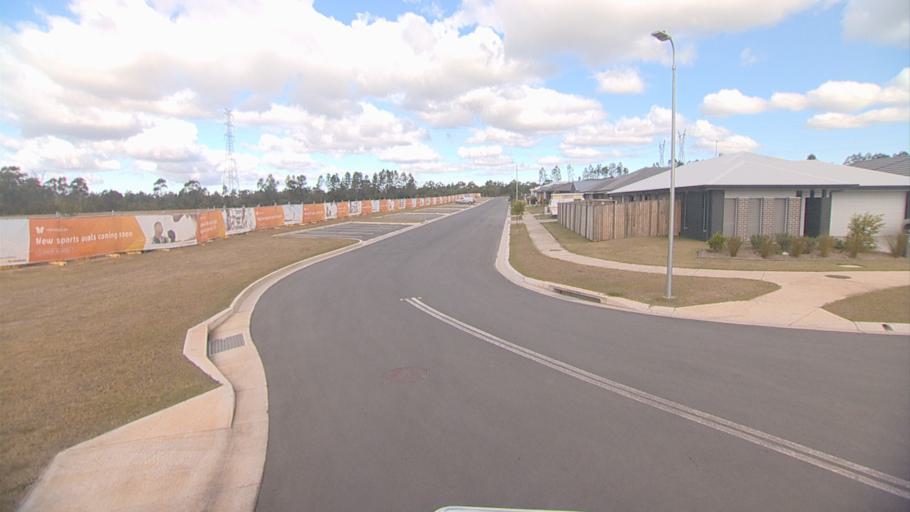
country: AU
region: Queensland
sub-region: Logan
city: Chambers Flat
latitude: -27.8109
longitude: 153.1170
